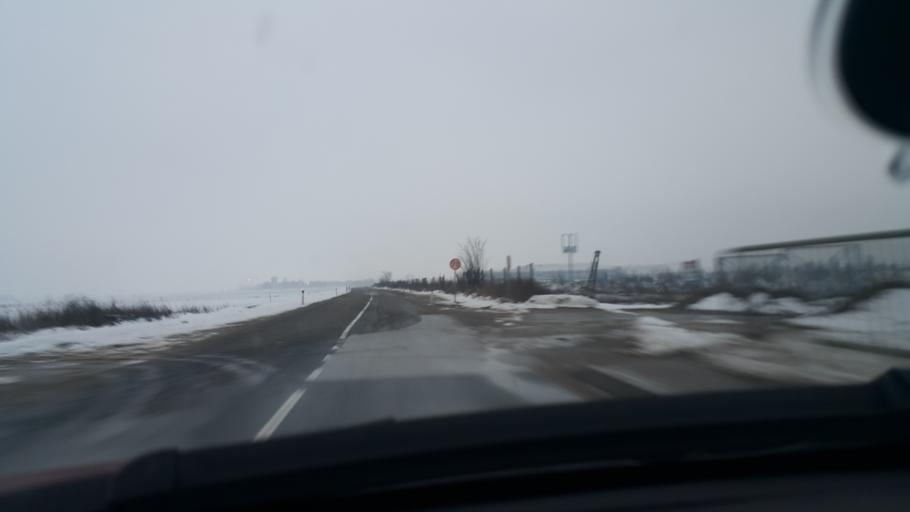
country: SI
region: Hoce-Slivnica
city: Rogoza
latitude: 46.4885
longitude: 15.6739
